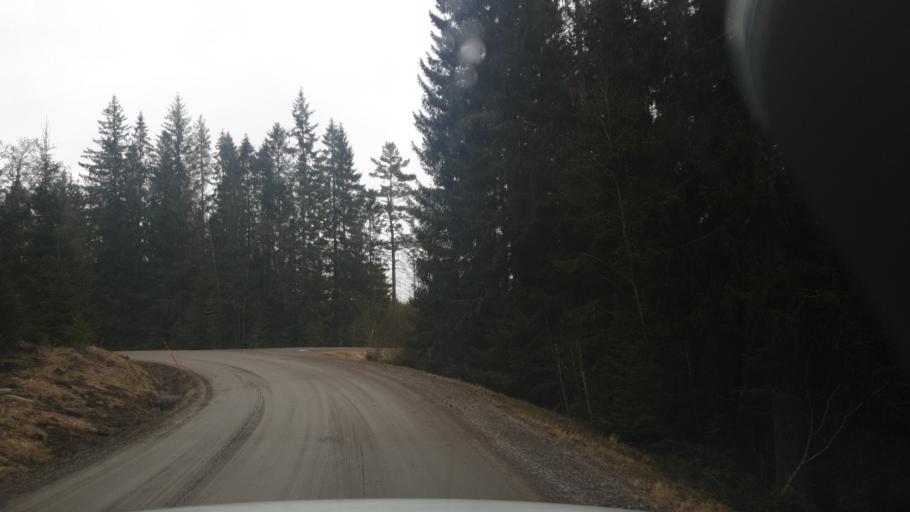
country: NO
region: Ostfold
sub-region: Romskog
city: Romskog
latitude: 59.7118
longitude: 12.0289
